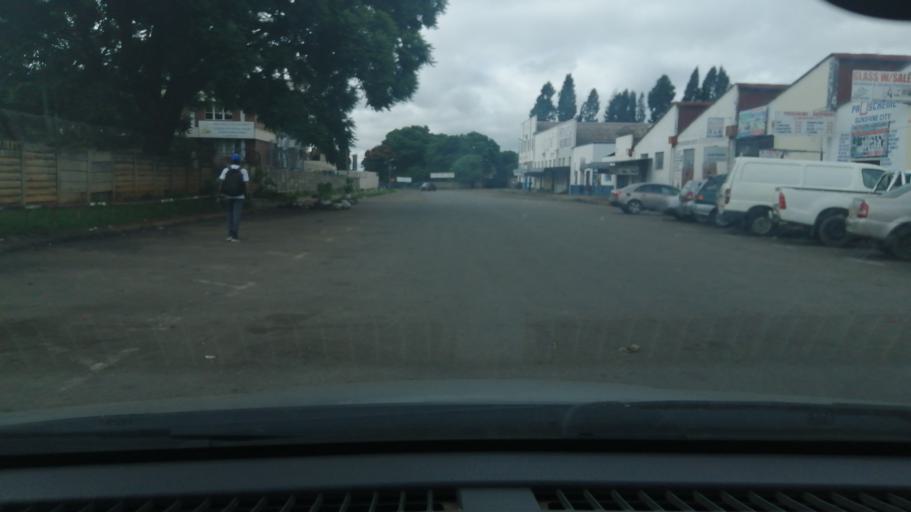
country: ZW
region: Harare
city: Harare
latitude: -17.8403
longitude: 31.0423
